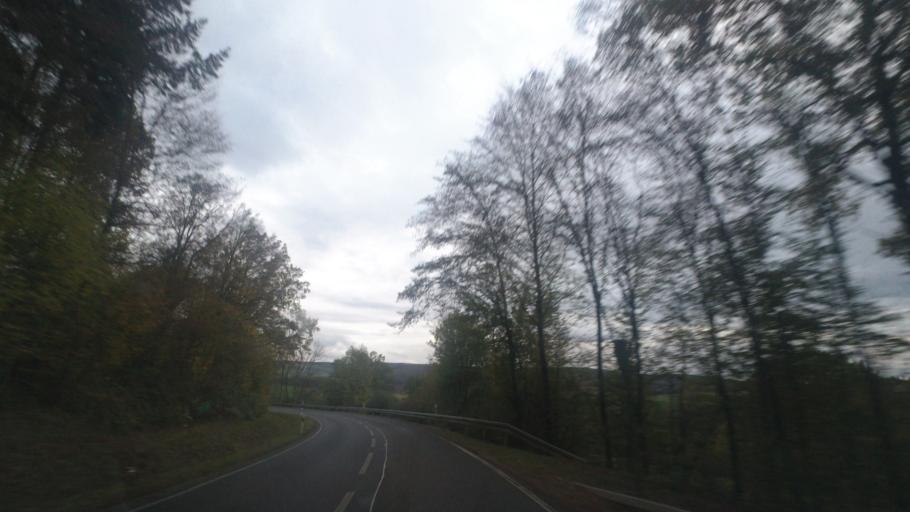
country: DE
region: Hesse
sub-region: Regierungsbezirk Darmstadt
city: Steinau an der Strasse
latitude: 50.3245
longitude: 9.4269
